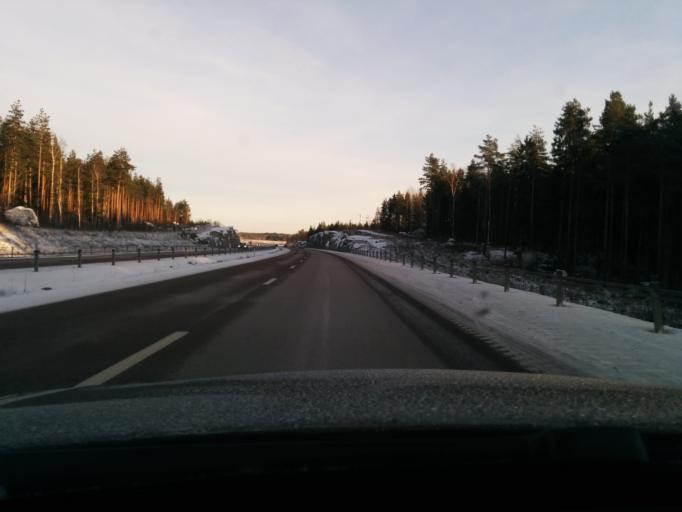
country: SE
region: Uppsala
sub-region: Enkopings Kommun
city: Hummelsta
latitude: 59.6399
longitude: 16.9510
